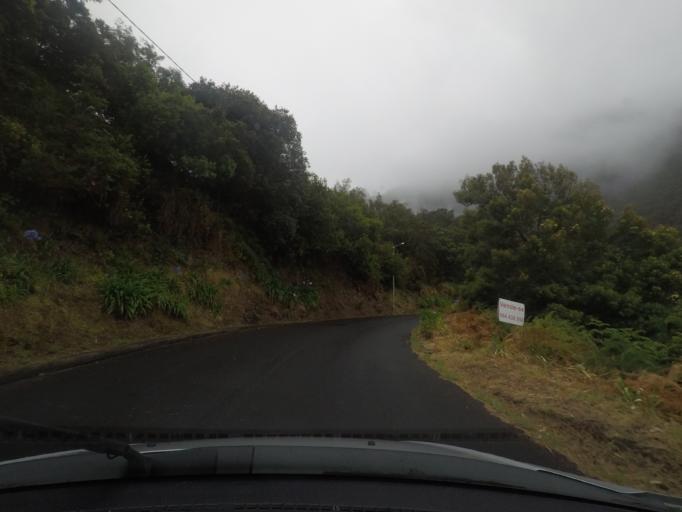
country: PT
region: Madeira
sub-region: Santana
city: Santana
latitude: 32.7842
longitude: -16.8592
